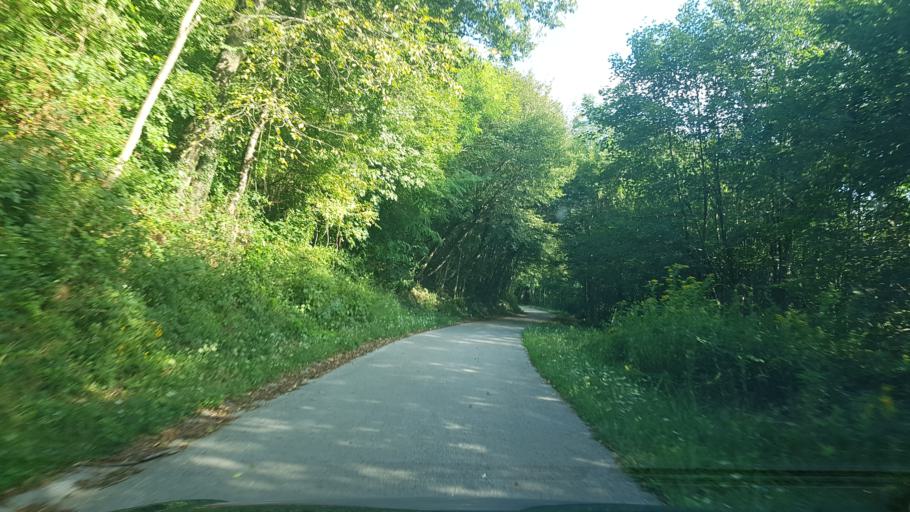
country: SI
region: Kanal
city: Deskle
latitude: 46.0258
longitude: 13.6145
